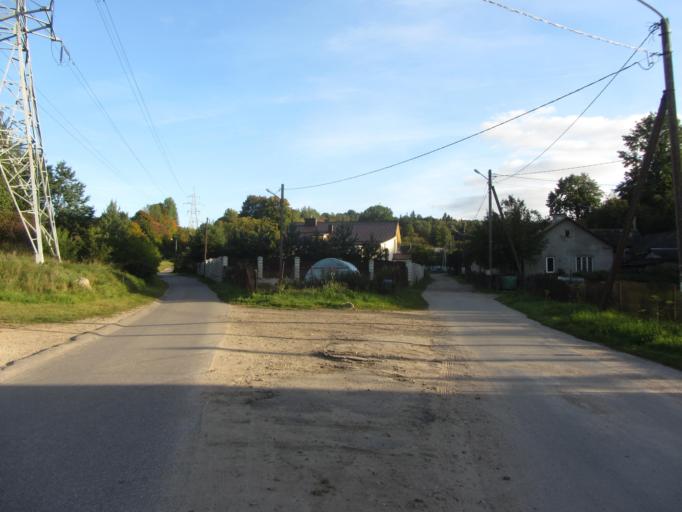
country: LT
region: Vilnius County
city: Lazdynai
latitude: 54.6402
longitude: 25.2113
